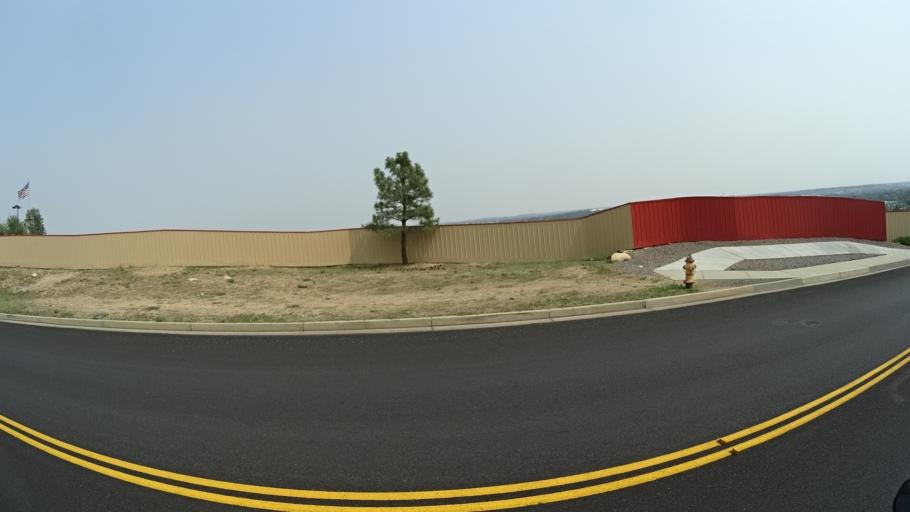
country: US
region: Colorado
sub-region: El Paso County
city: Colorado Springs
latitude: 38.8173
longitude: -104.8390
